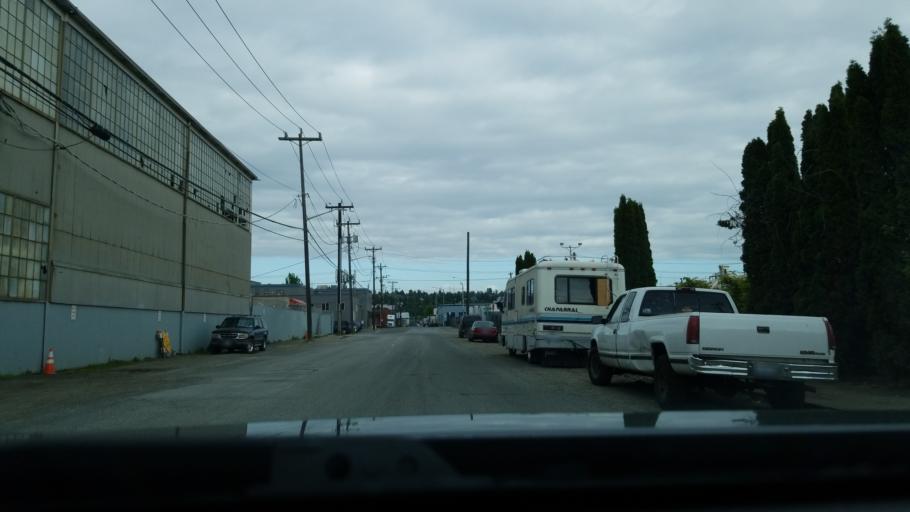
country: US
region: Washington
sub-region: King County
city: White Center
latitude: 47.5574
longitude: -122.3366
